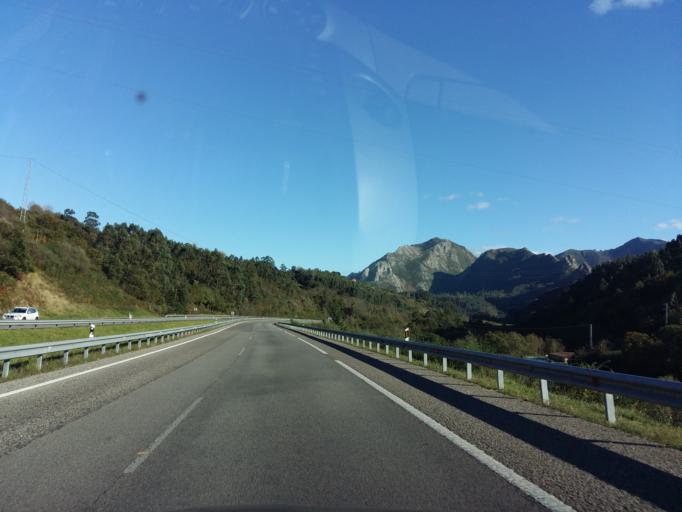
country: ES
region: Asturias
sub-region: Province of Asturias
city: Ribadesella
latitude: 43.4402
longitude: -5.0844
